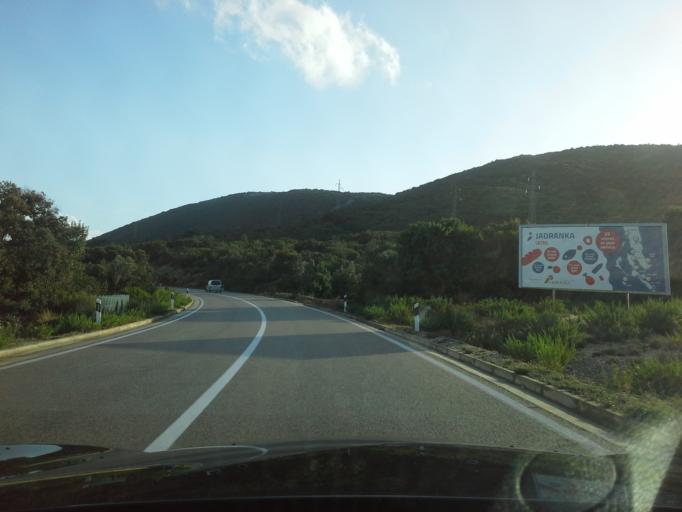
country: HR
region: Primorsko-Goranska
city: Mali Losinj
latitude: 44.6475
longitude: 14.3910
